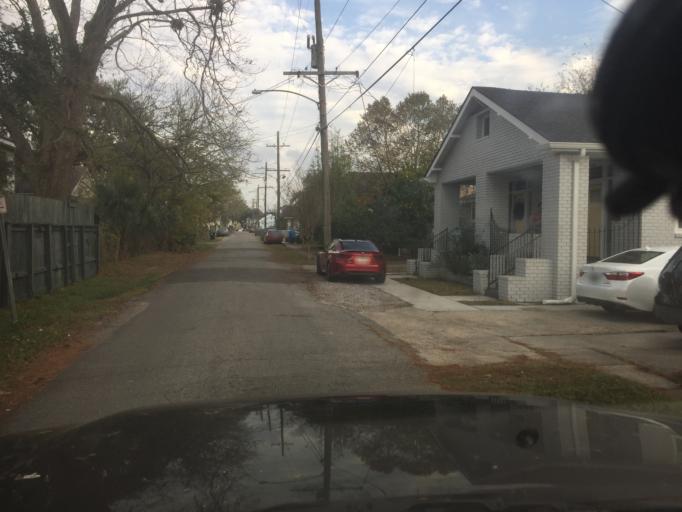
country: US
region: Louisiana
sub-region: Orleans Parish
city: New Orleans
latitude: 29.9866
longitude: -90.0793
